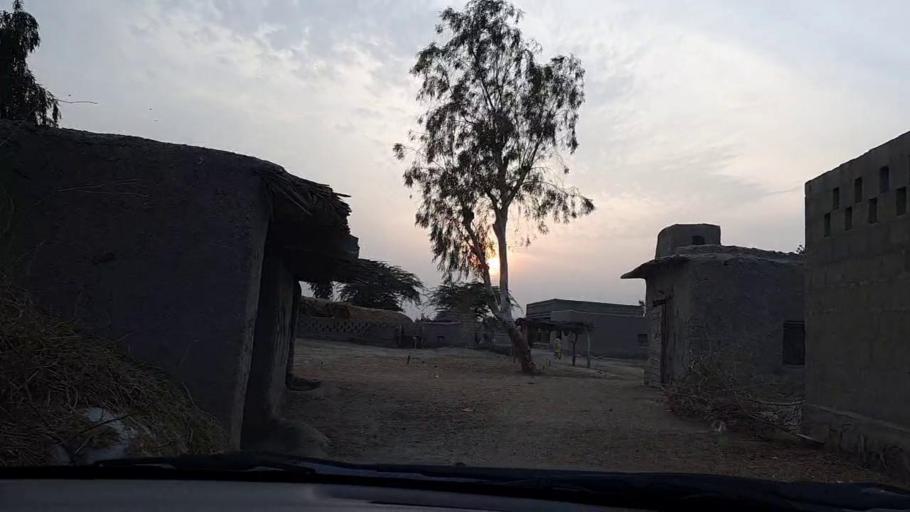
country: PK
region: Sindh
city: Thatta
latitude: 24.7810
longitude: 67.9465
